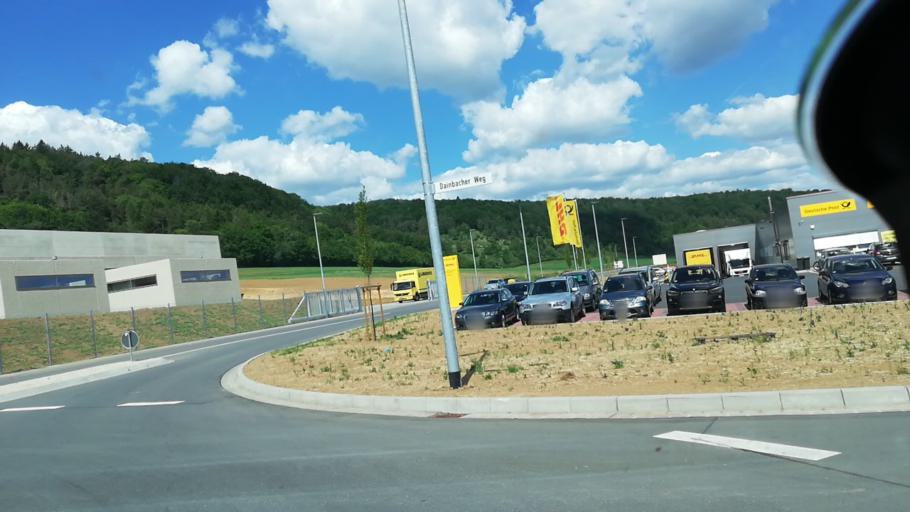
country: DE
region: Baden-Wuerttemberg
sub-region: Regierungsbezirk Stuttgart
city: Bad Mergentheim
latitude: 49.4961
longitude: 9.7509
